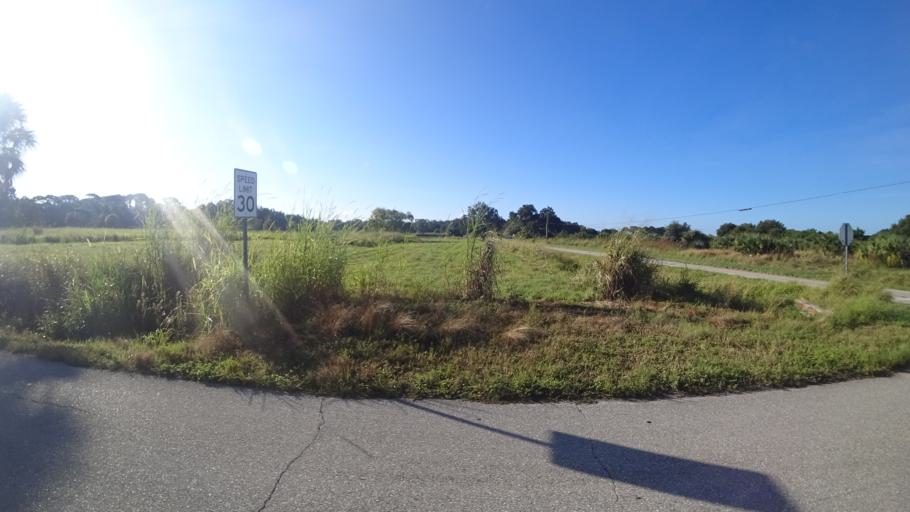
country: US
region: Florida
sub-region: Manatee County
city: Memphis
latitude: 27.5682
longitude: -82.5479
